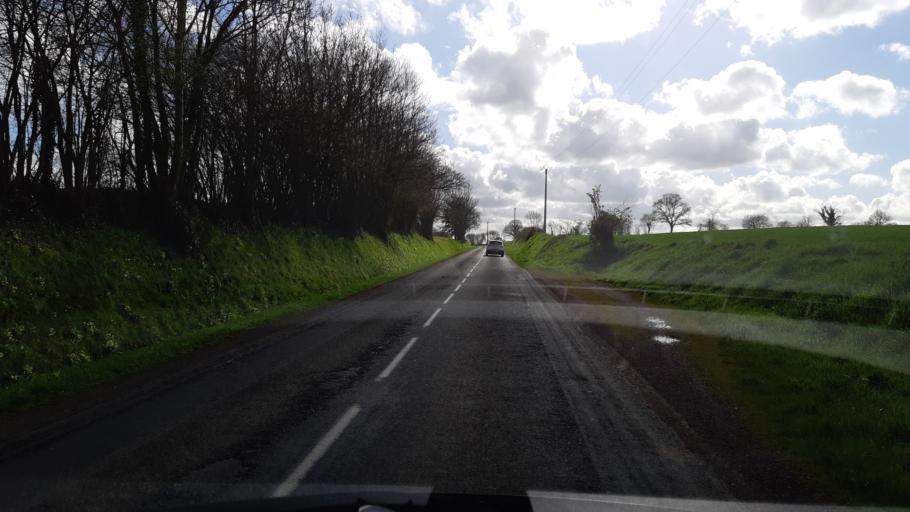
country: FR
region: Lower Normandy
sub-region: Departement de la Manche
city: Agneaux
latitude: 49.0247
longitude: -1.1557
